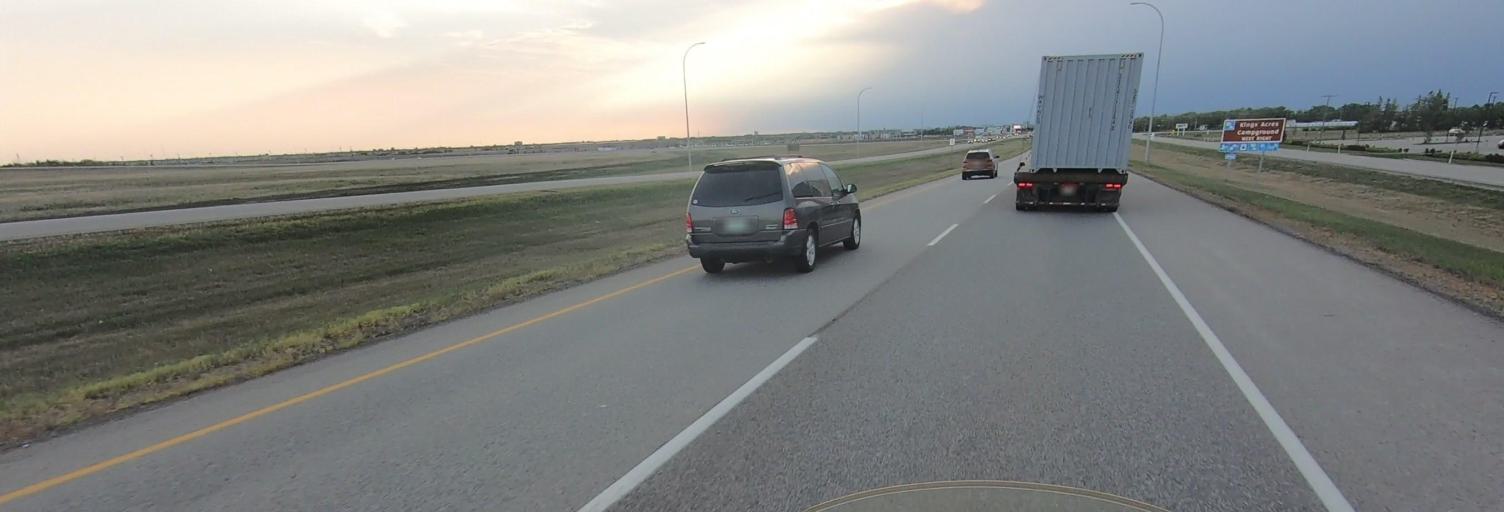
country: CA
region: Saskatchewan
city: Pilot Butte
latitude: 50.4476
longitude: -104.4956
